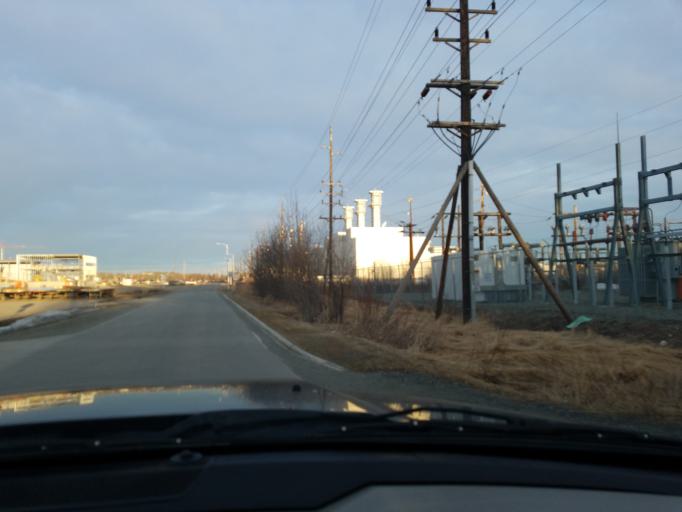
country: US
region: Alaska
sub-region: Anchorage Municipality
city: Anchorage
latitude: 61.1664
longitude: -149.9010
